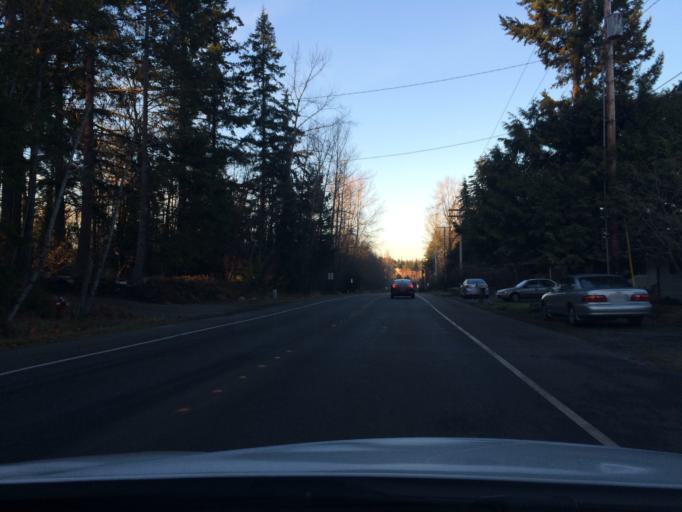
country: US
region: Washington
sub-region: Whatcom County
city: Geneva
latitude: 48.7549
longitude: -122.4225
